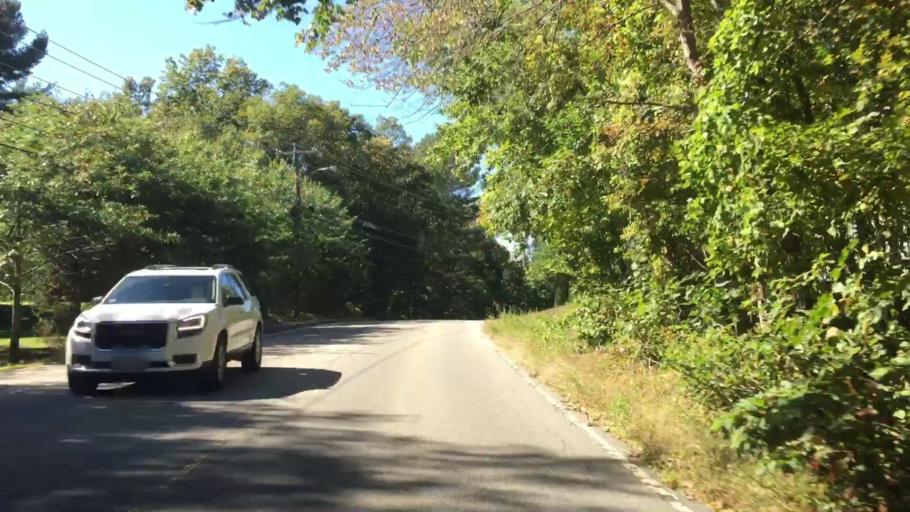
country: US
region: Massachusetts
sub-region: Essex County
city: North Andover
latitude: 42.6828
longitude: -71.0865
